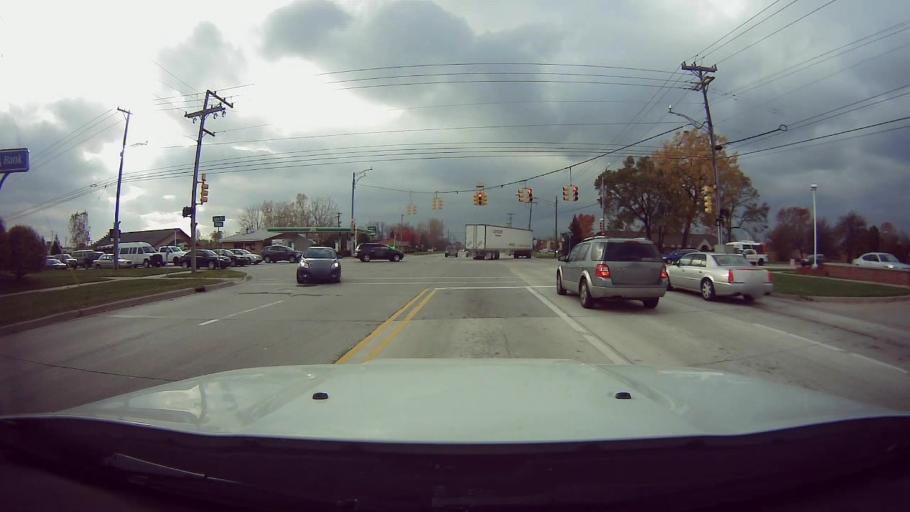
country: US
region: Michigan
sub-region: Oakland County
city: Clawson
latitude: 42.5493
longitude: -83.1060
